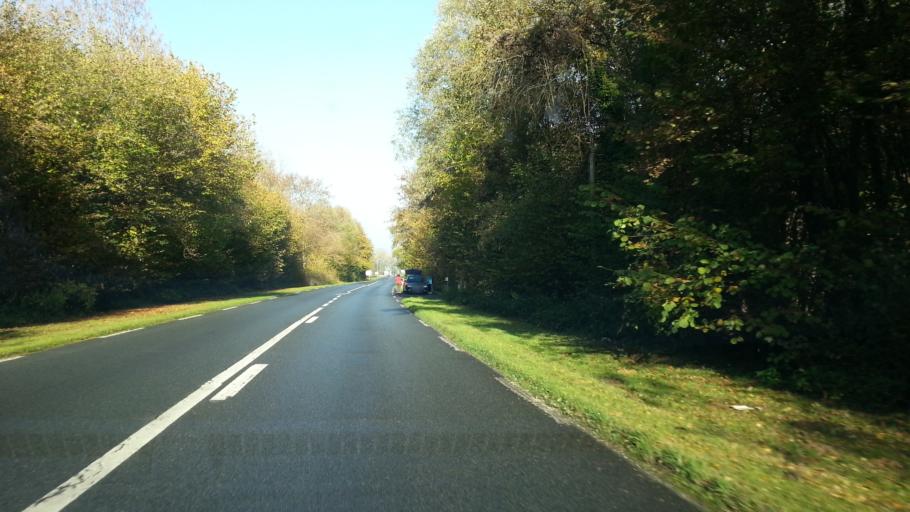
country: FR
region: Picardie
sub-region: Departement de l'Oise
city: Balagny-sur-Therain
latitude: 49.3056
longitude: 2.3293
